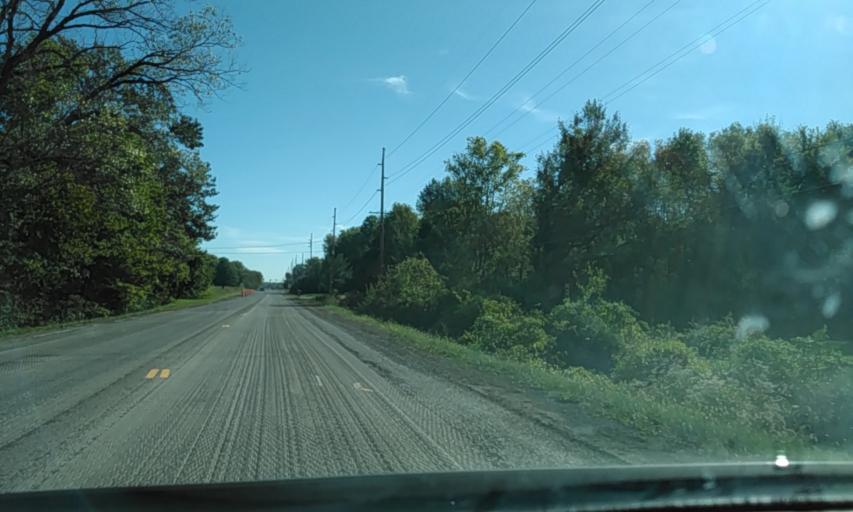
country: US
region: Illinois
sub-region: Madison County
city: Troy
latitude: 38.7177
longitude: -89.8621
